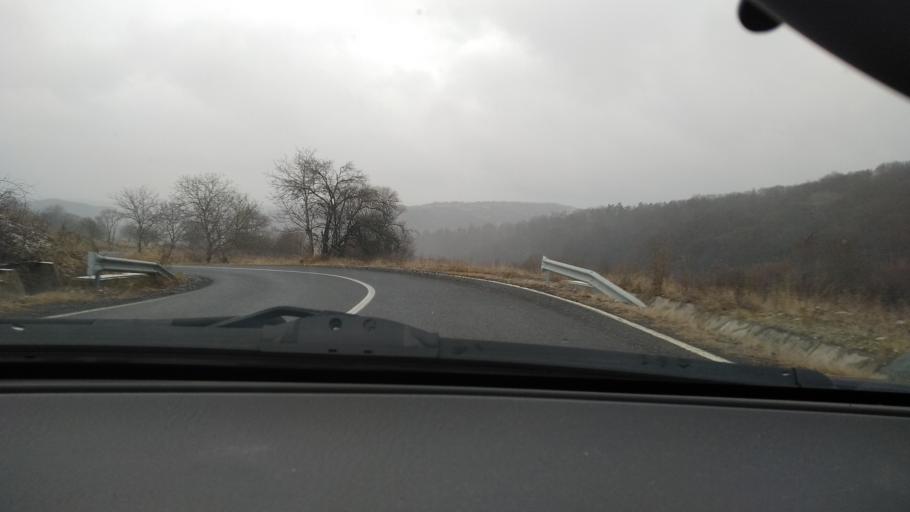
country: RO
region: Mures
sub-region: Comuna Chibed
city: Chibed
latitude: 46.5809
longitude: 24.9561
